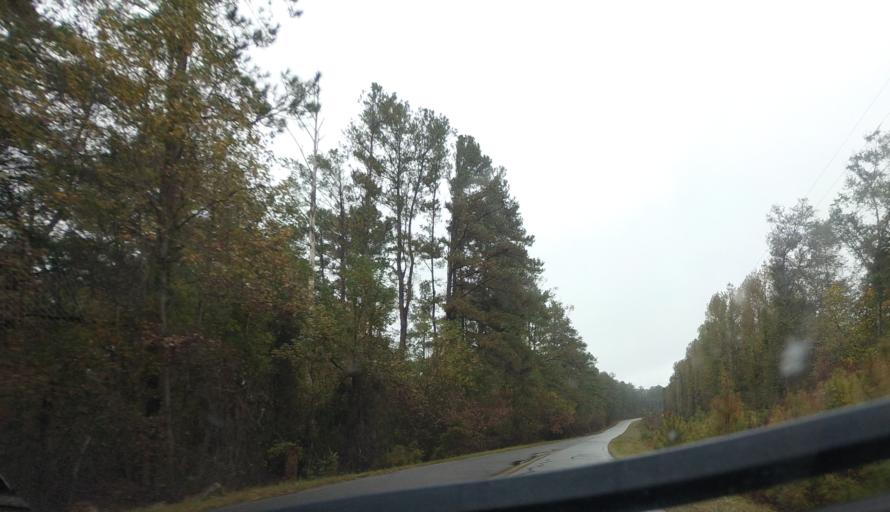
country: US
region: Georgia
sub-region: Peach County
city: Fort Valley
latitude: 32.5393
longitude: -83.9293
